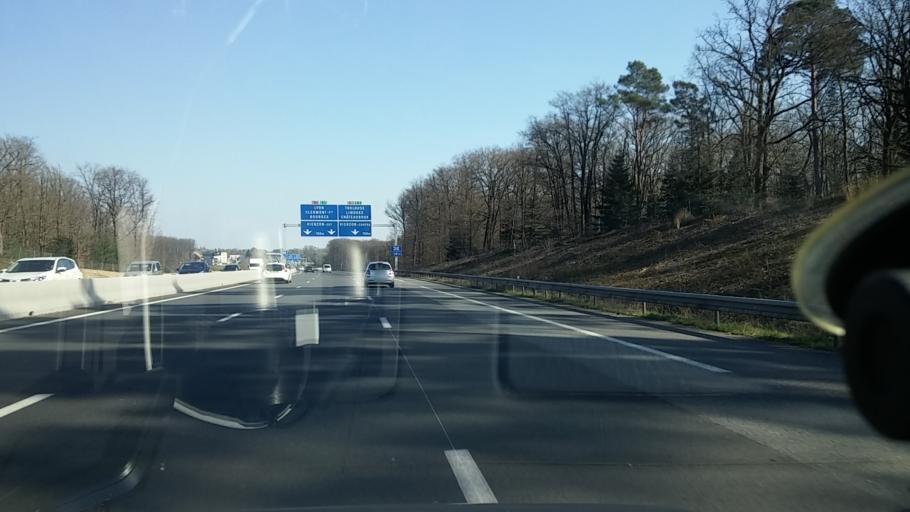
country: FR
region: Centre
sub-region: Departement du Cher
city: Vierzon
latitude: 47.2500
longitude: 2.0571
